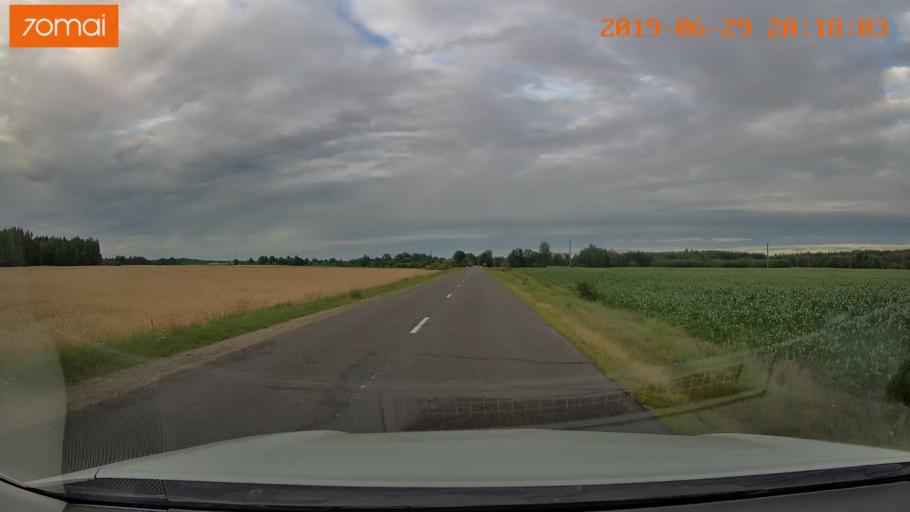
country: BY
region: Brest
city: Asnyezhytsy
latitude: 52.3922
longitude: 26.2285
